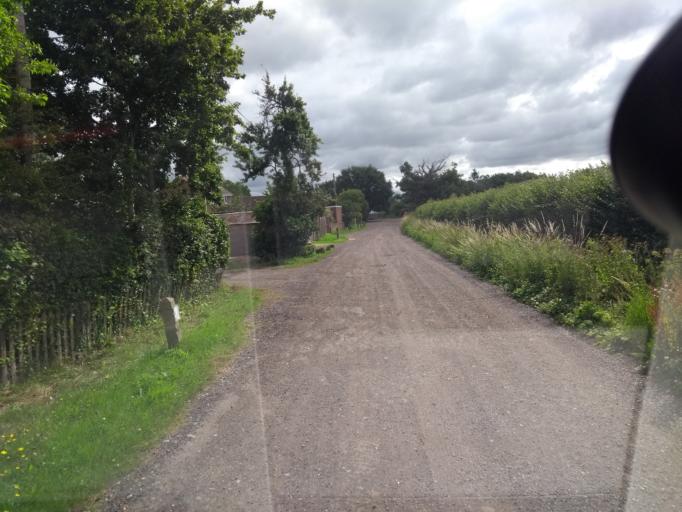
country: GB
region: England
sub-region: Somerset
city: Creech Saint Michael
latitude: 51.0321
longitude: -3.0307
